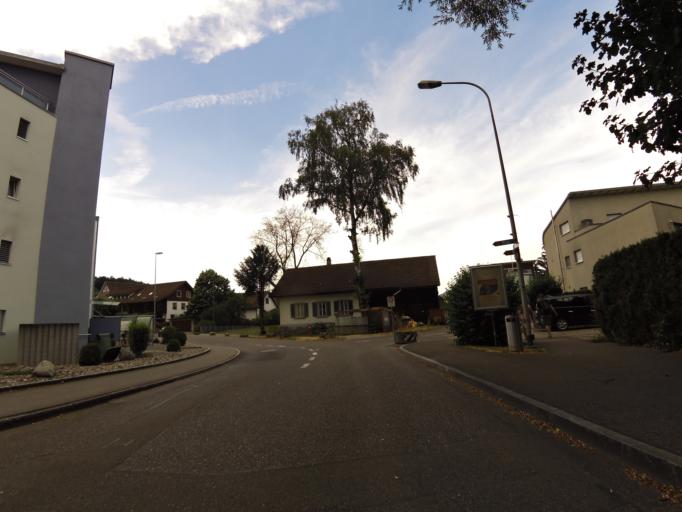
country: CH
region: Aargau
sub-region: Bezirk Aarau
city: Suhr
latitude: 47.3739
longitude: 8.0821
